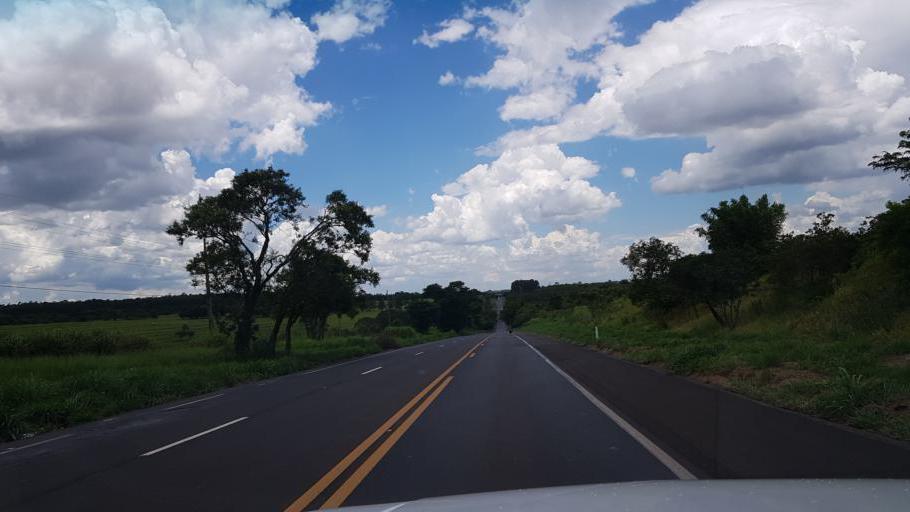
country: BR
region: Sao Paulo
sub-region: Paraguacu Paulista
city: Paraguacu Paulista
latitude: -22.3897
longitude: -50.6121
